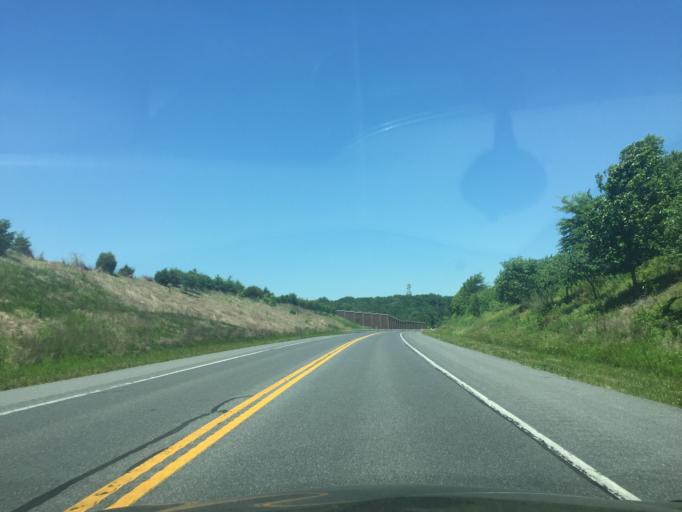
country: US
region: Maryland
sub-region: Carroll County
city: Hampstead
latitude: 39.5983
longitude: -76.8629
